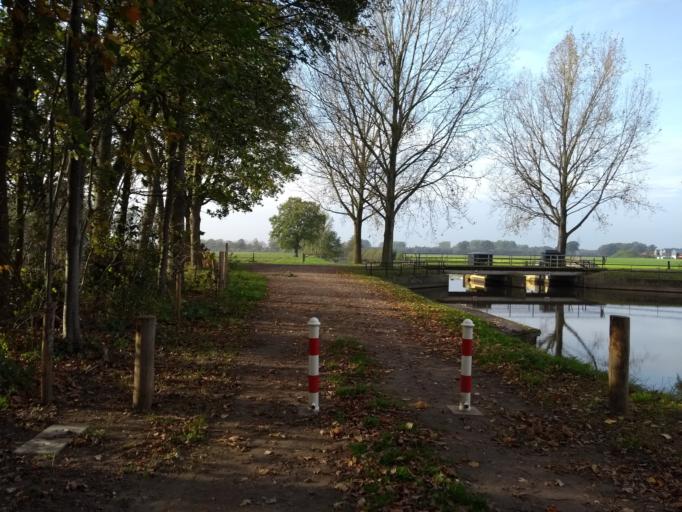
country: NL
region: Overijssel
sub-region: Gemeente Almelo
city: Almelo
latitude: 52.3884
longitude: 6.6724
